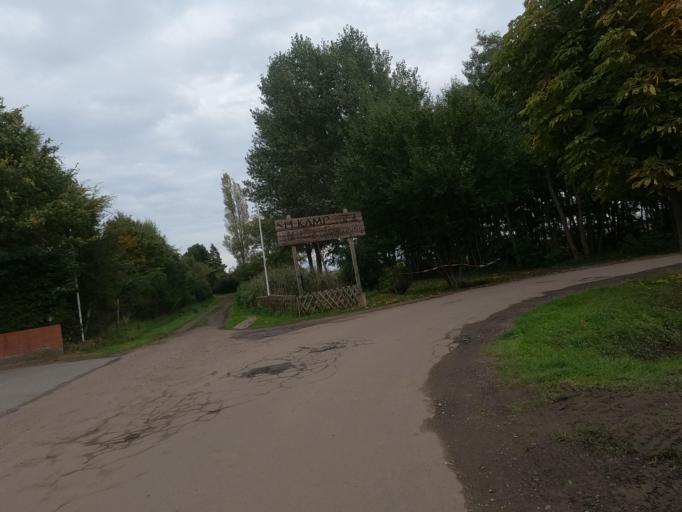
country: DE
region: Schleswig-Holstein
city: Grossenbrode
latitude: 54.3447
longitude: 11.0607
